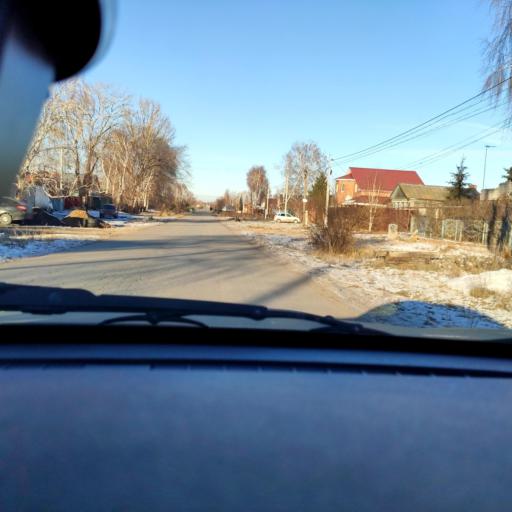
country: RU
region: Samara
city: Tol'yatti
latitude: 53.5576
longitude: 49.3980
